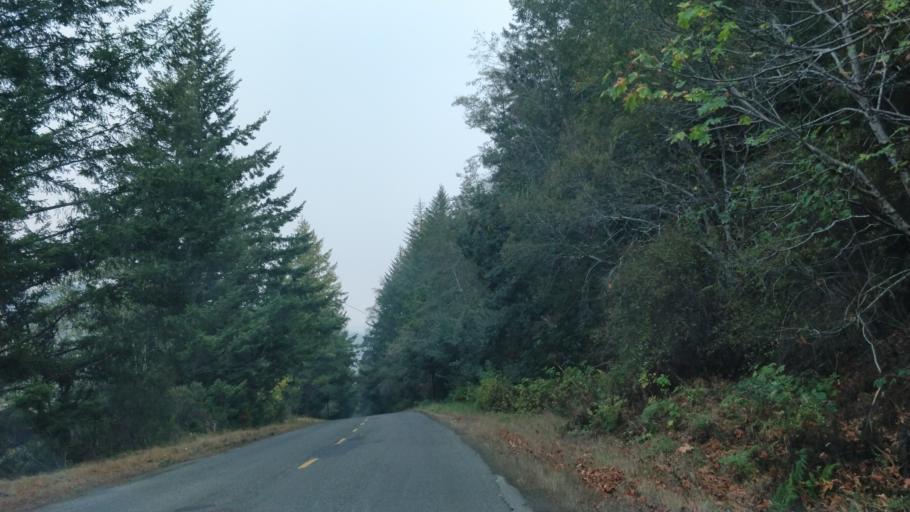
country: US
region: California
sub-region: Humboldt County
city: Rio Dell
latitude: 40.3107
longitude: -124.2746
